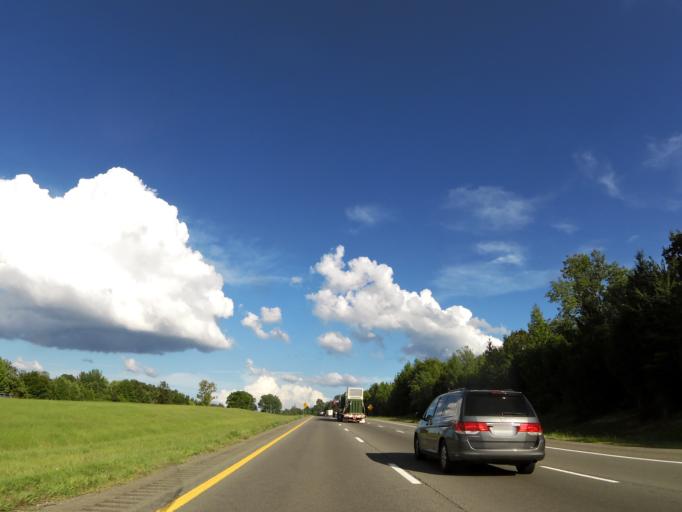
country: US
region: Tennessee
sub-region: Robertson County
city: Coopertown
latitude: 36.3291
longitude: -86.8957
